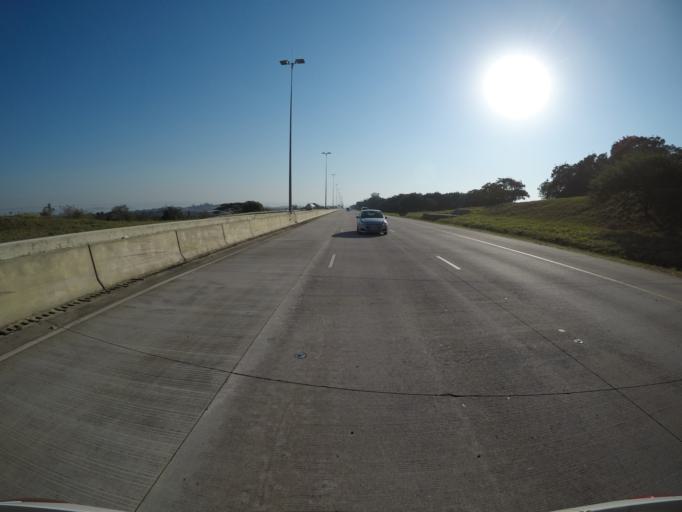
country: ZA
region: KwaZulu-Natal
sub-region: iLembe District Municipality
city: Ballitoville
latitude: -29.6065
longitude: 31.1367
